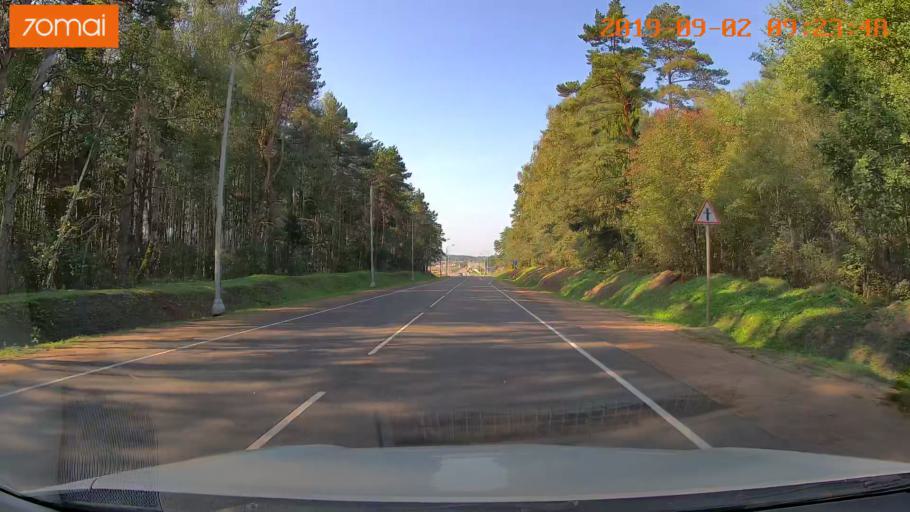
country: RU
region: Kaluga
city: Yukhnov
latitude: 54.7722
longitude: 35.3069
